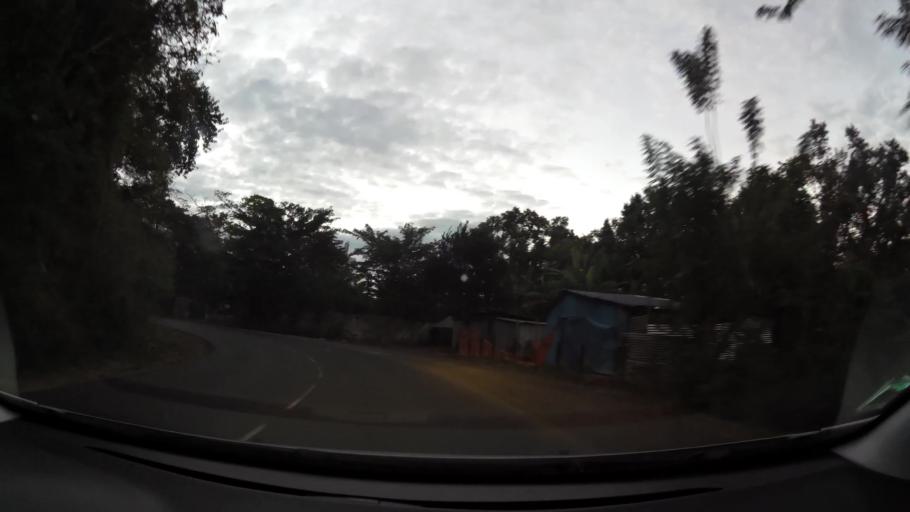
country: YT
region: Bandraboua
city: Bandraboua
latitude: -12.7317
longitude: 45.1371
